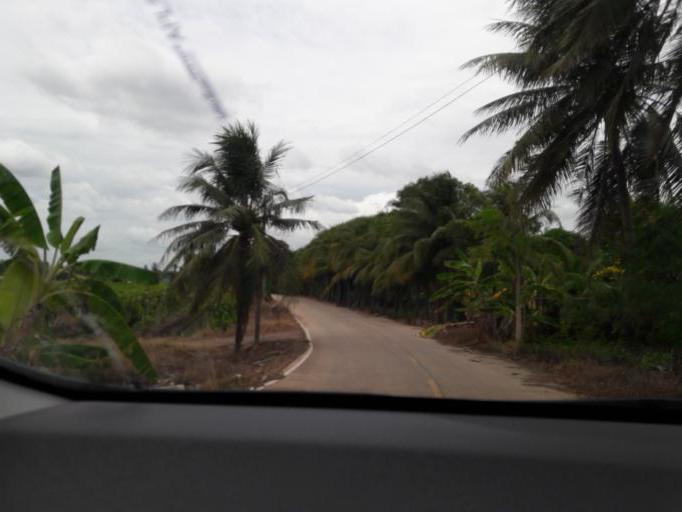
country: TH
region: Ratchaburi
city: Damnoen Saduak
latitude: 13.5583
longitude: 100.0184
